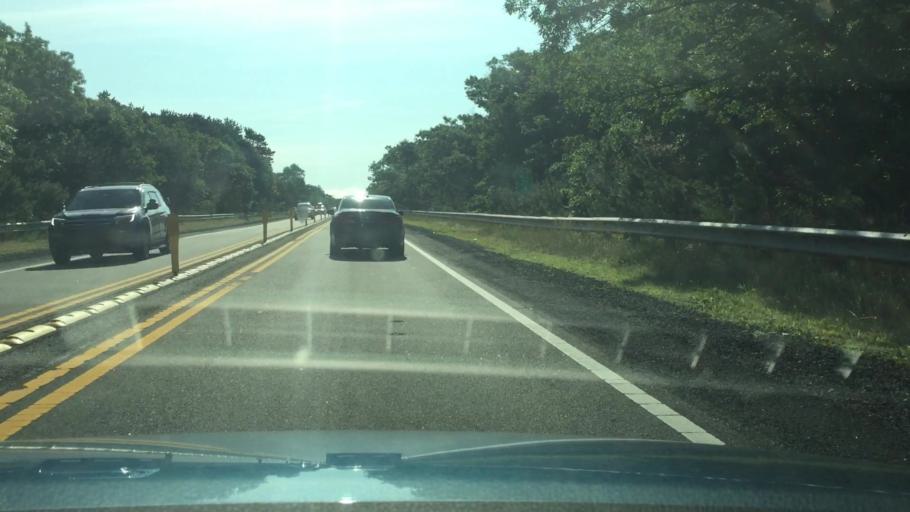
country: US
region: Massachusetts
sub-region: Barnstable County
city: Northwest Harwich
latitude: 41.7008
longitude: -70.1230
